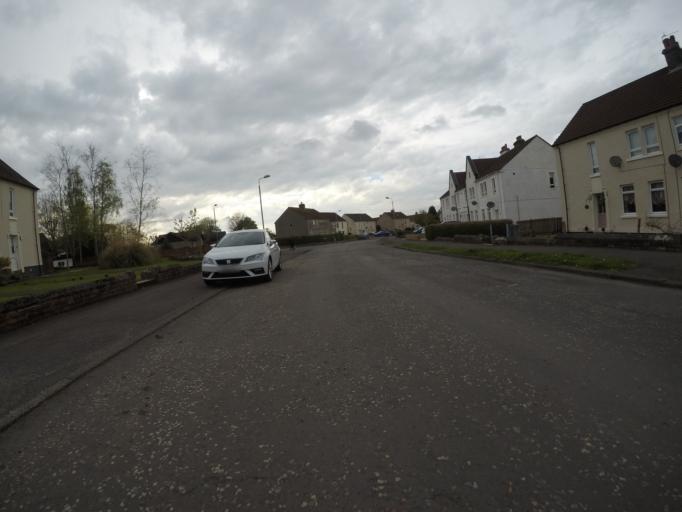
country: GB
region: Scotland
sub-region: East Ayrshire
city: Kilmaurs
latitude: 55.6400
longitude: -4.5323
